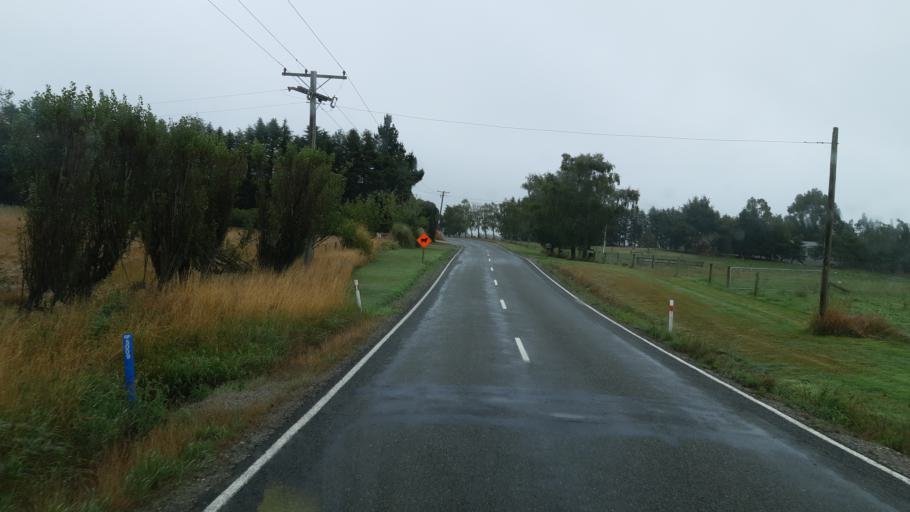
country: NZ
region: Otago
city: Oamaru
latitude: -44.9293
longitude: 170.7918
